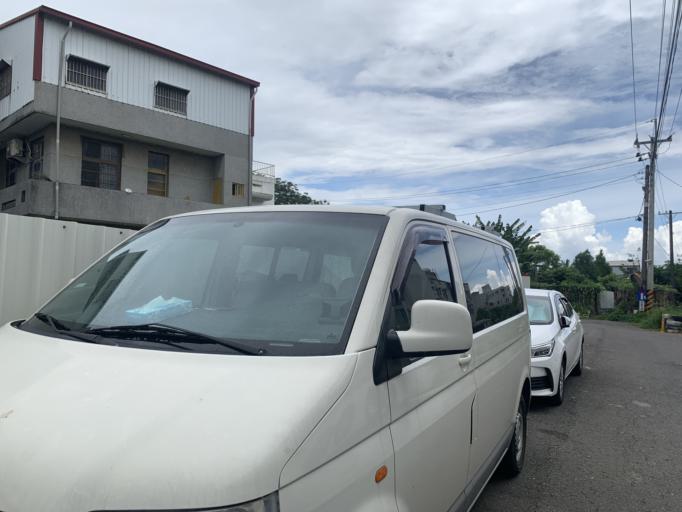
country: TW
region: Taiwan
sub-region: Chiayi
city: Jiayi Shi
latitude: 23.4907
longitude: 120.4800
